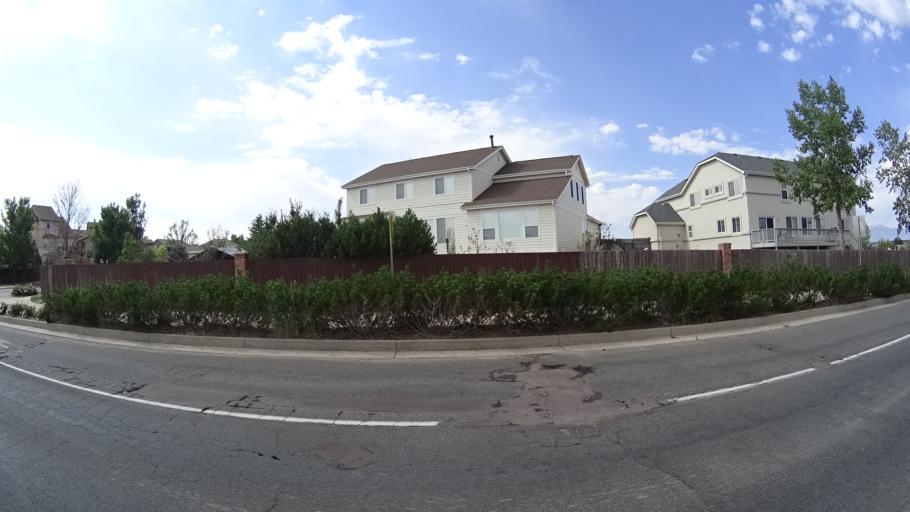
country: US
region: Colorado
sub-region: El Paso County
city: Cimarron Hills
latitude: 38.9118
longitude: -104.7006
